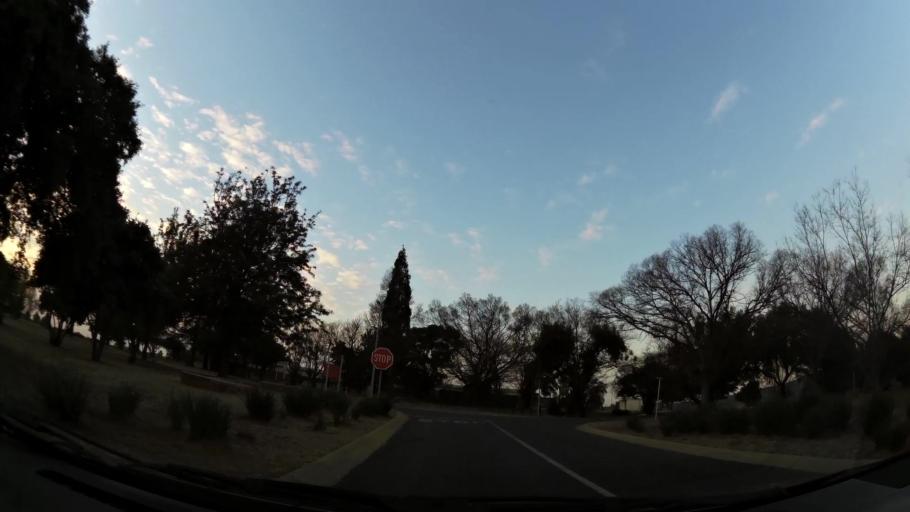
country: ZA
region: Gauteng
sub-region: City of Johannesburg Metropolitan Municipality
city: Diepsloot
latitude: -26.0030
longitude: 28.0468
